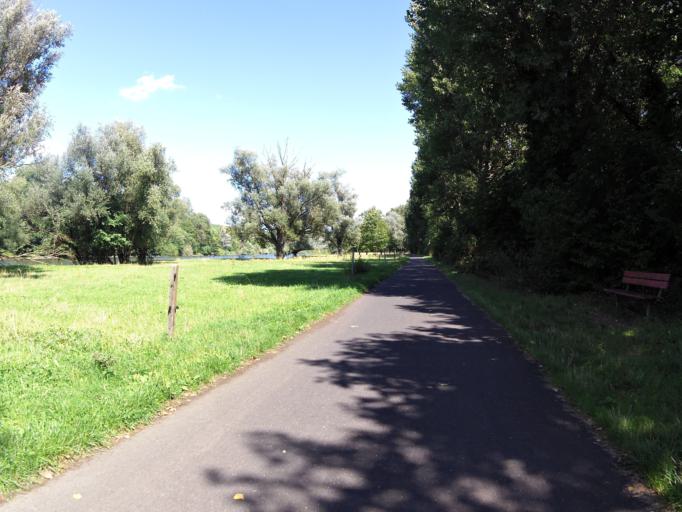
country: DE
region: Bavaria
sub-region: Regierungsbezirk Unterfranken
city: Ochsenfurt
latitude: 49.6664
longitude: 10.0712
